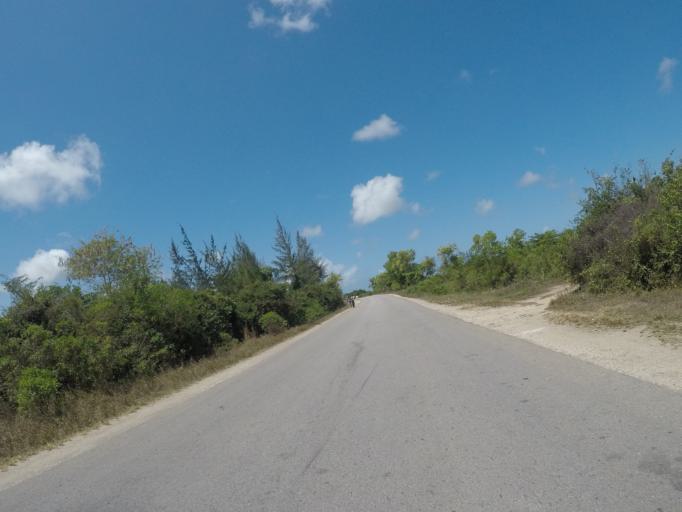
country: TZ
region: Zanzibar Central/South
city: Nganane
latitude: -6.2823
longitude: 39.4709
